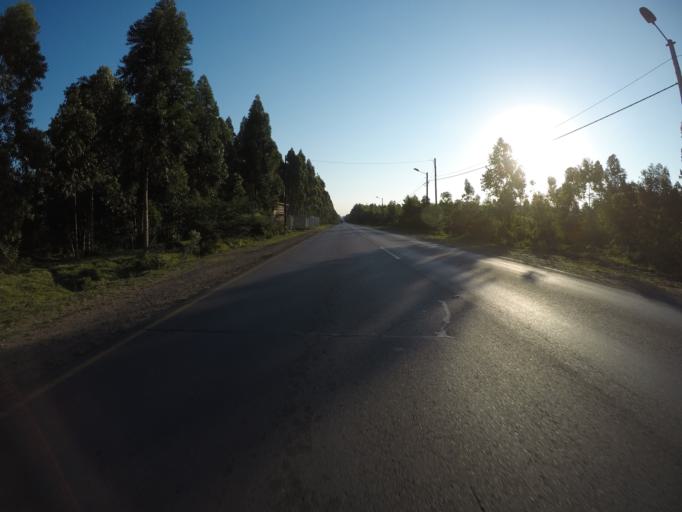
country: ZA
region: KwaZulu-Natal
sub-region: uThungulu District Municipality
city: KwaMbonambi
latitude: -28.6831
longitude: 32.1883
